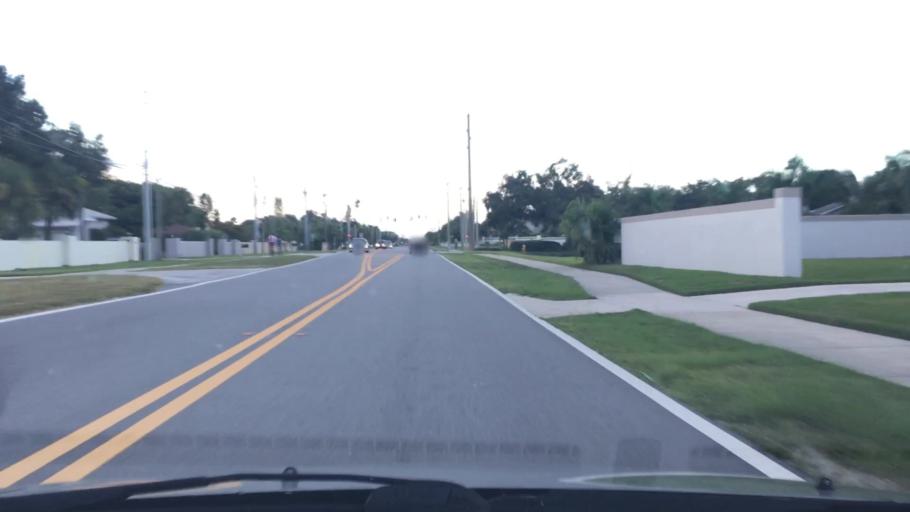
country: US
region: Florida
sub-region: Brevard County
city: Indian Harbour Beach
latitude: 28.1197
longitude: -80.5874
